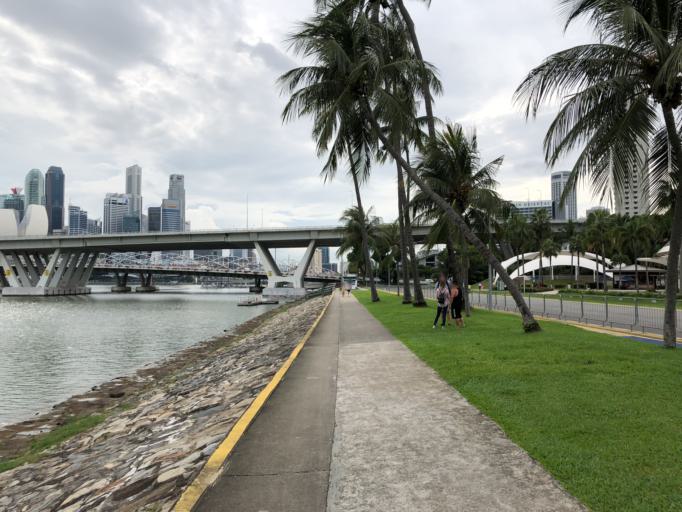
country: SG
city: Singapore
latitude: 1.2885
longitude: 103.8635
